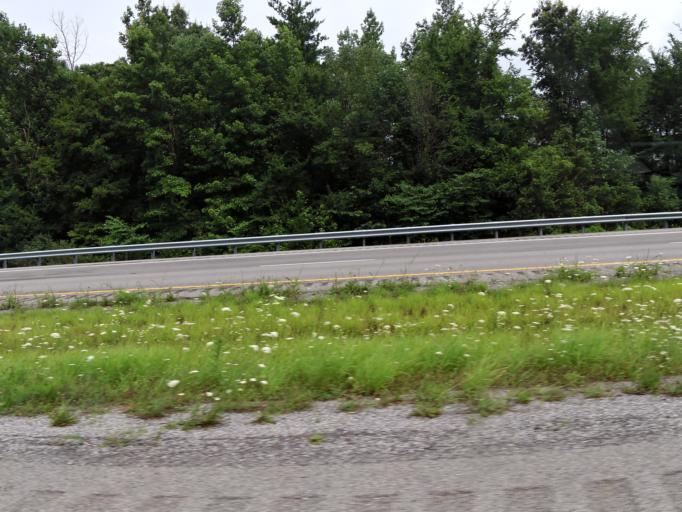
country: US
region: Kentucky
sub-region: Muhlenberg County
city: Central City
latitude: 37.3158
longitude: -87.0496
